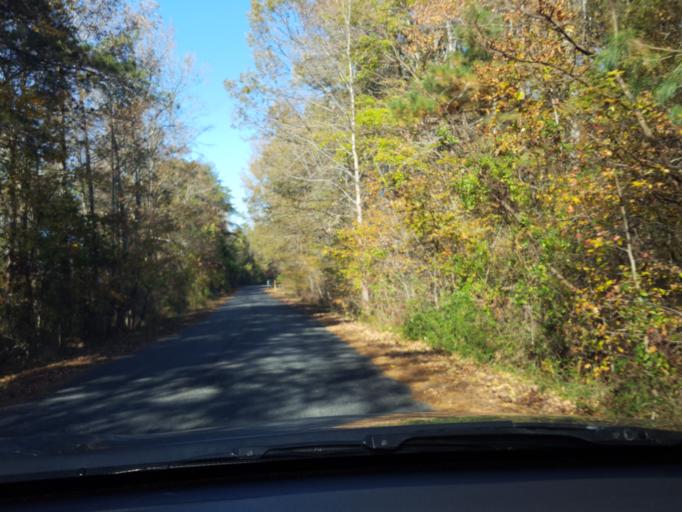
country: US
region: Maryland
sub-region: Saint Mary's County
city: California
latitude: 38.2489
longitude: -76.5415
